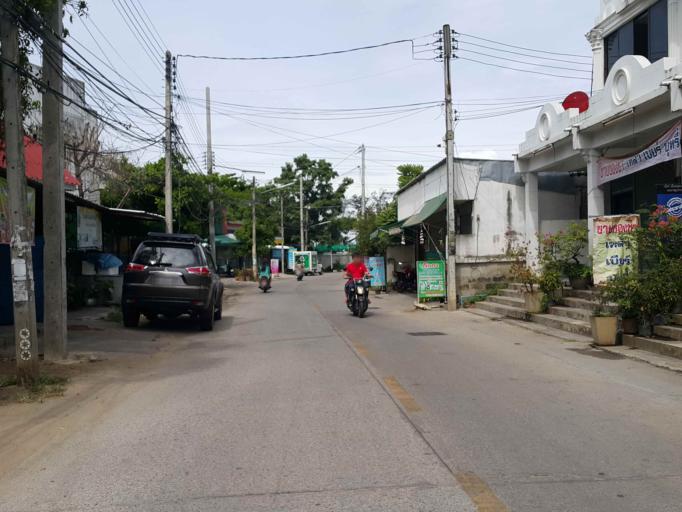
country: TH
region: Chiang Mai
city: Chiang Mai
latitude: 18.7637
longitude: 99.0102
